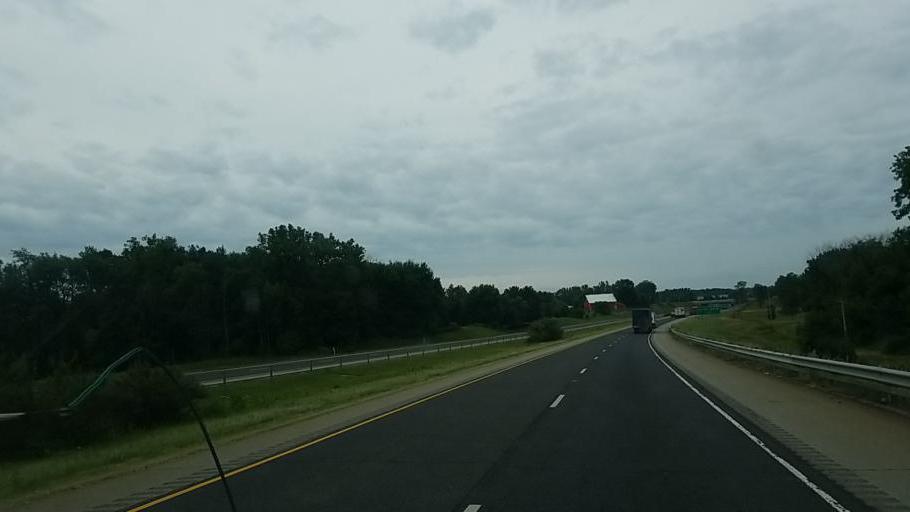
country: US
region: Indiana
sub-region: Steuben County
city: Angola
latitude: 41.6764
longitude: -85.0057
